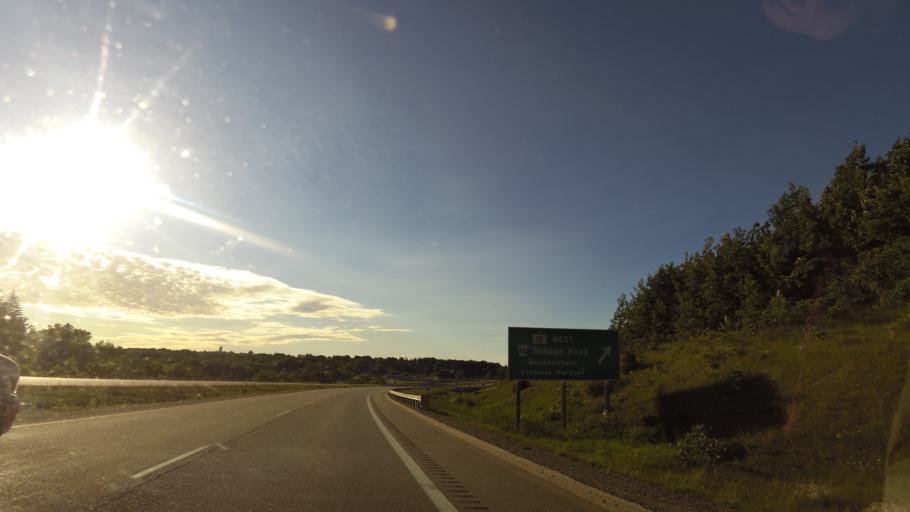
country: CA
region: Ontario
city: Midland
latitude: 44.7442
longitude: -79.6994
